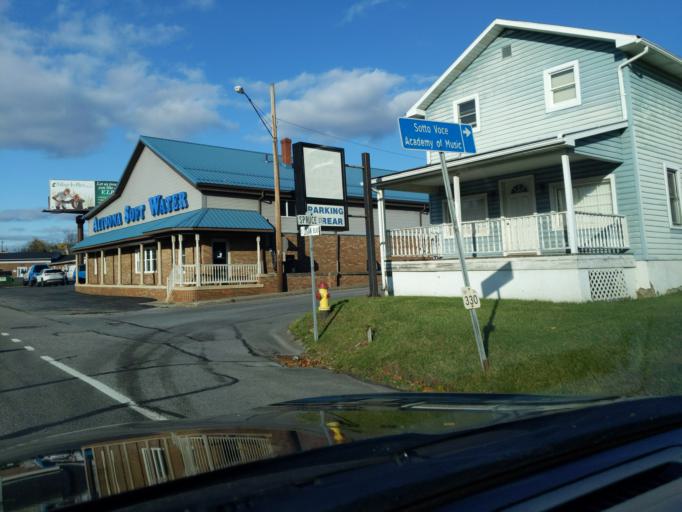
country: US
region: Pennsylvania
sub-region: Blair County
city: Lakemont
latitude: 40.4613
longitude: -78.3952
